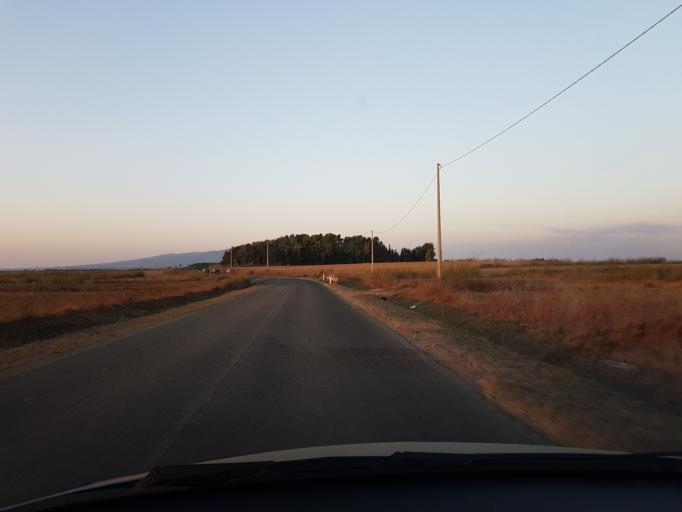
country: IT
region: Sardinia
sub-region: Provincia di Oristano
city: Nurachi
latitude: 39.9866
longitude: 8.4583
